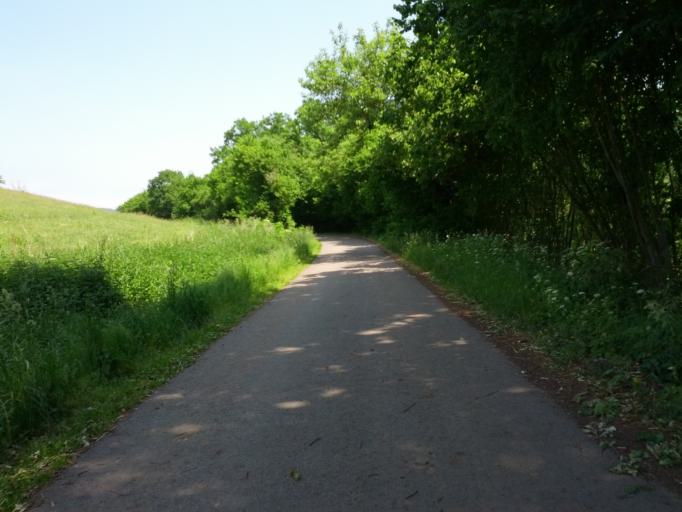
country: DE
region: Thuringia
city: Wiesenthal
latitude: 50.7226
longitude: 10.1627
